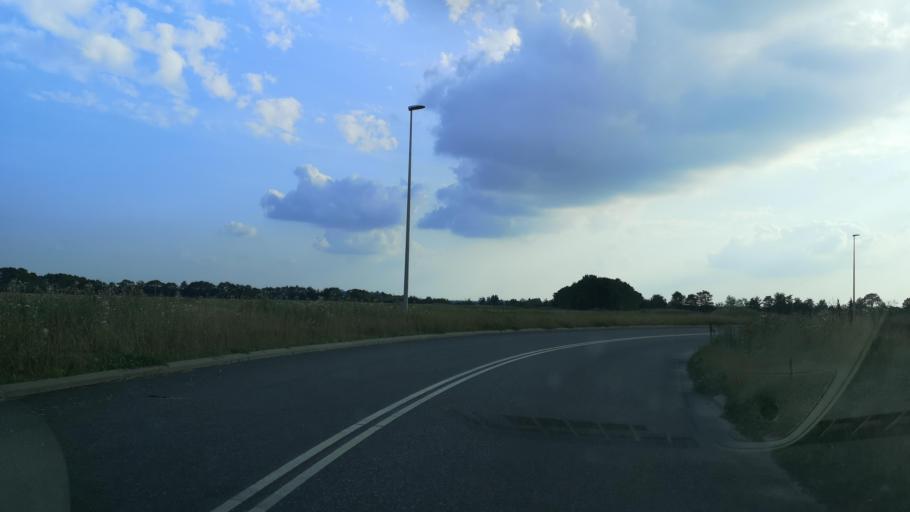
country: DK
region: Central Jutland
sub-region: Herning Kommune
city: Snejbjerg
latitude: 56.1176
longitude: 8.9291
